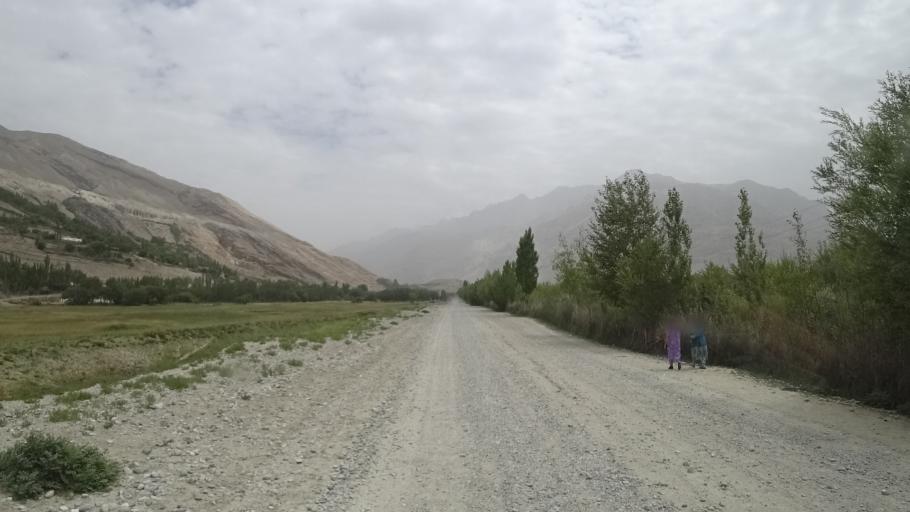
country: AF
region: Badakhshan
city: Khandud
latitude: 37.0353
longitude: 72.6410
